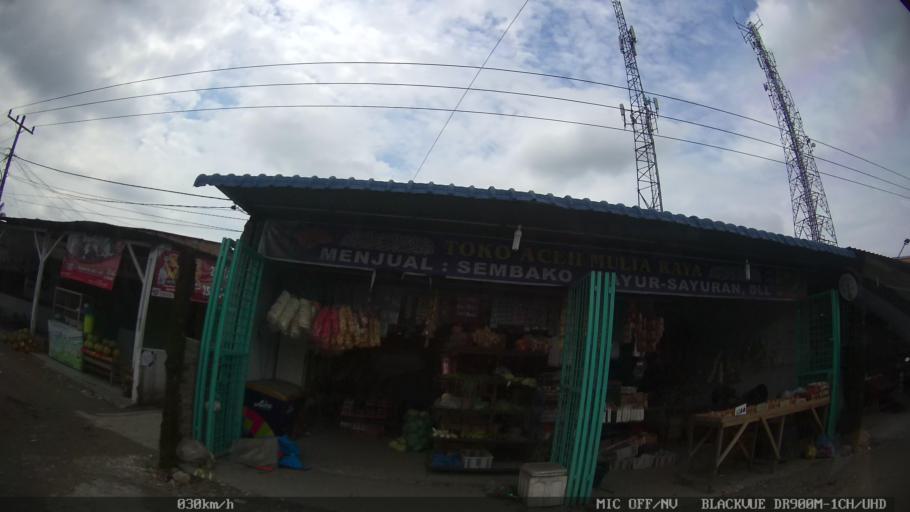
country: ID
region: North Sumatra
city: Sunggal
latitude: 3.6183
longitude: 98.6187
